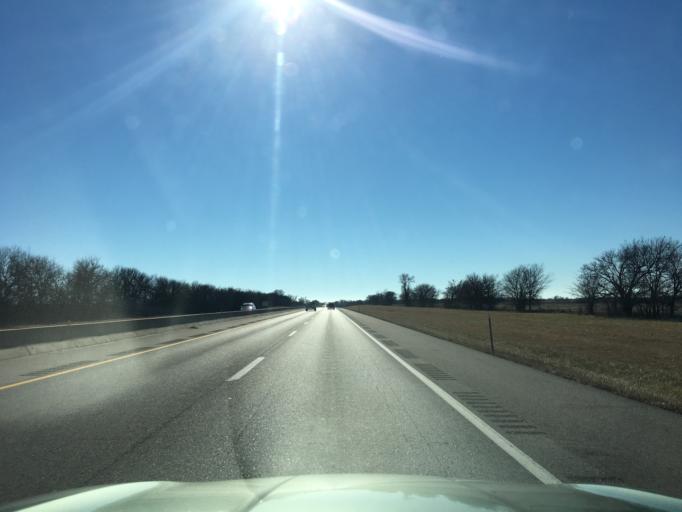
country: US
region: Kansas
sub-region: Sumner County
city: Wellington
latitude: 37.1000
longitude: -97.3387
